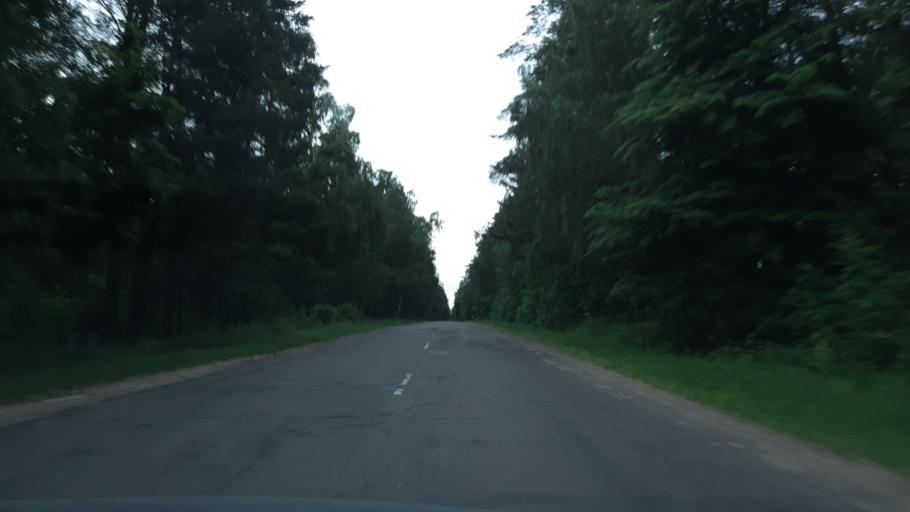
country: BY
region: Minsk
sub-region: Smalyavitski Rayon
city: Oktjabr'skij
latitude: 54.1113
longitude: 28.1964
